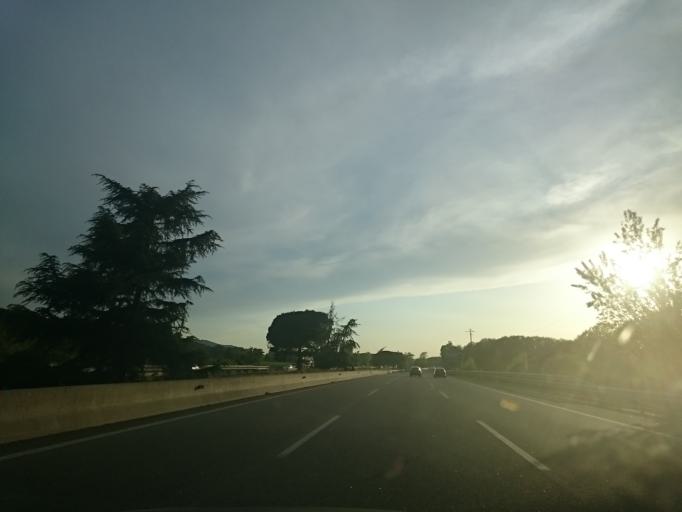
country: ES
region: Catalonia
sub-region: Provincia de Barcelona
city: Llinars del Valles
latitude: 41.6497
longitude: 2.4370
